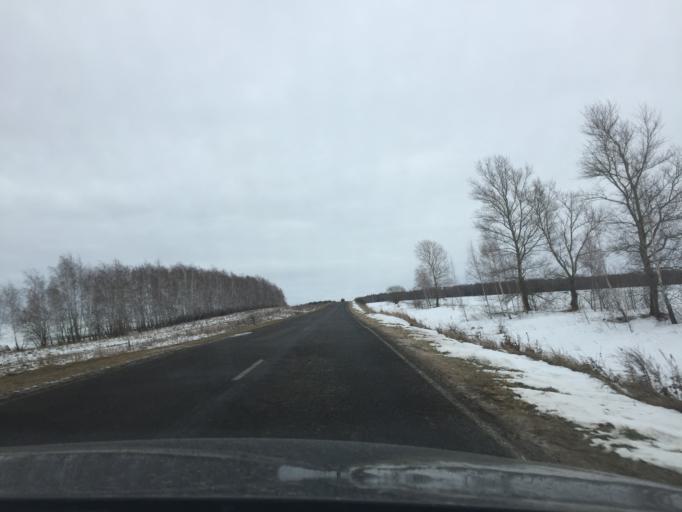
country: RU
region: Tula
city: Shchekino
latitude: 53.8152
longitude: 37.5348
